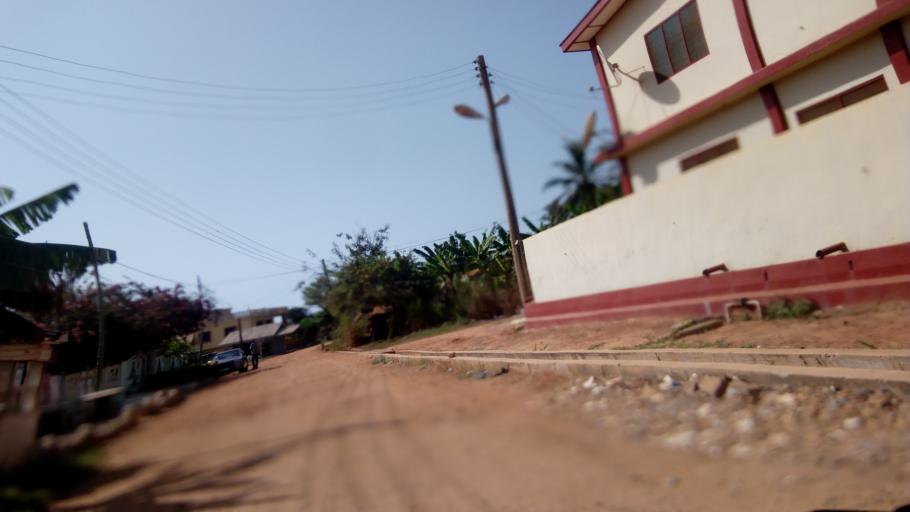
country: GH
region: Central
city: Cape Coast
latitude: 5.1175
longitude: -1.2700
